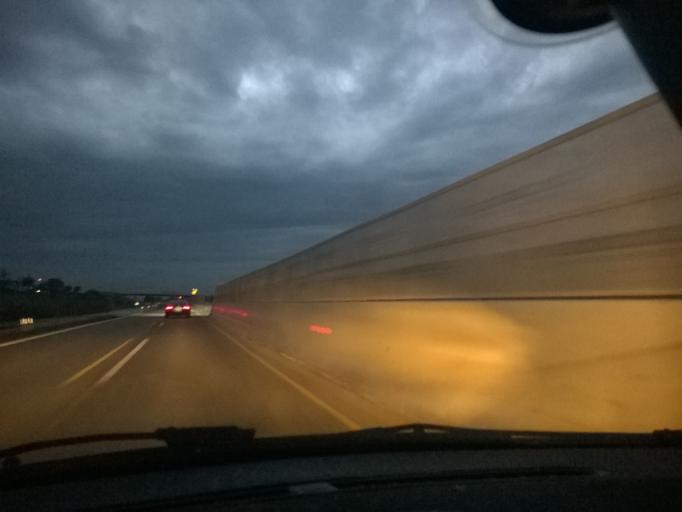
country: SI
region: Podlehnik
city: Podlehnik
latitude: 46.3556
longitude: 15.8681
